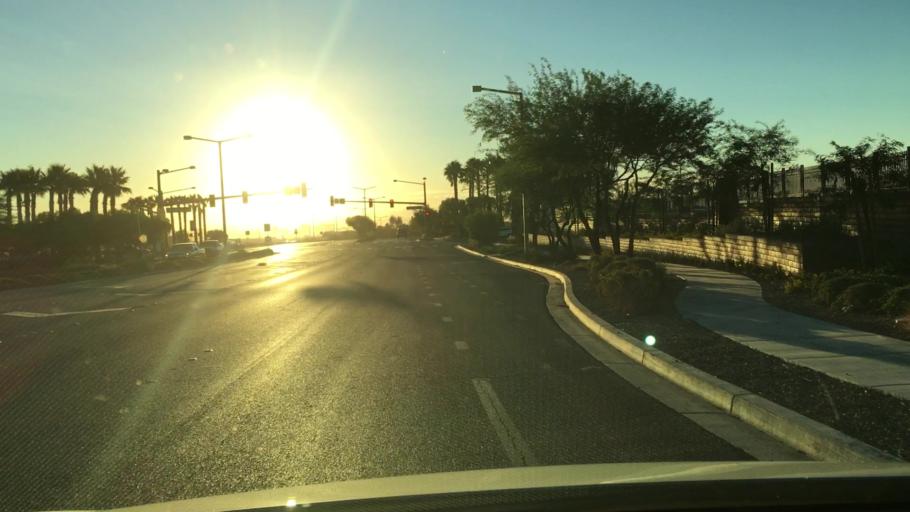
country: US
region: Nevada
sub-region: Clark County
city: Summerlin South
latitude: 36.1157
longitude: -115.3307
